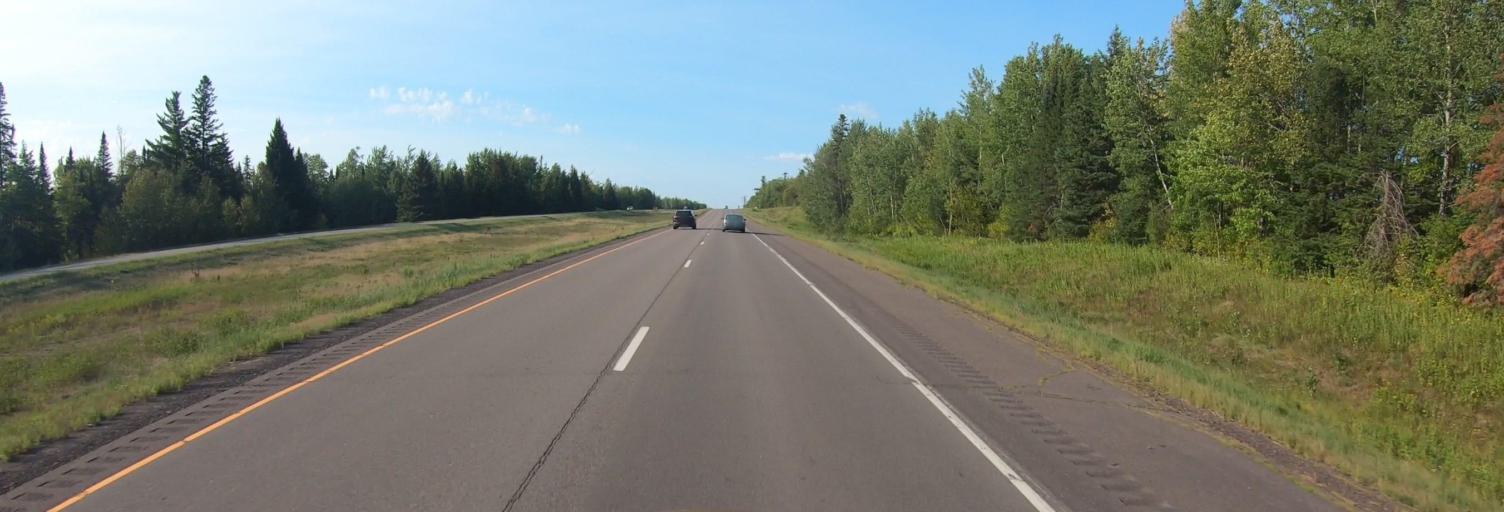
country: US
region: Minnesota
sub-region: Carlton County
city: Cloquet
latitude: 47.0035
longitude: -92.4709
